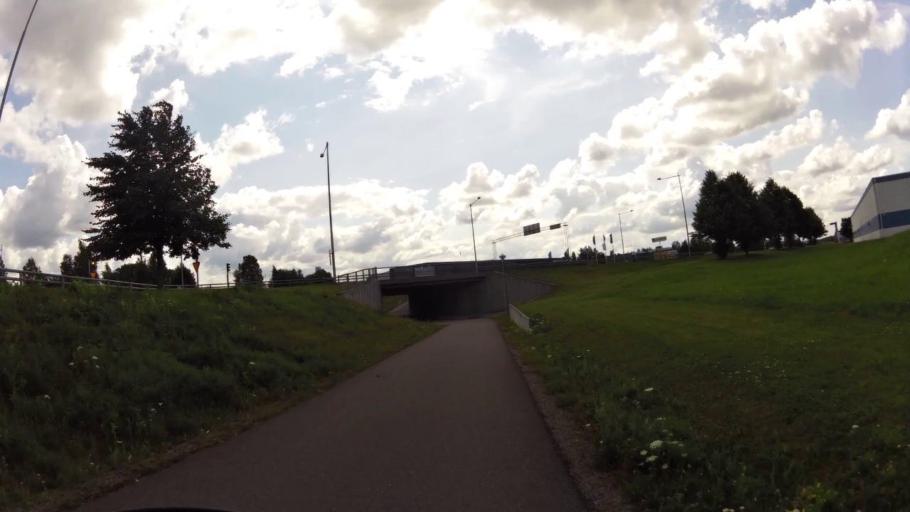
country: SE
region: OEstergoetland
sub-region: Linkopings Kommun
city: Linkoping
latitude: 58.4304
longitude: 15.5994
